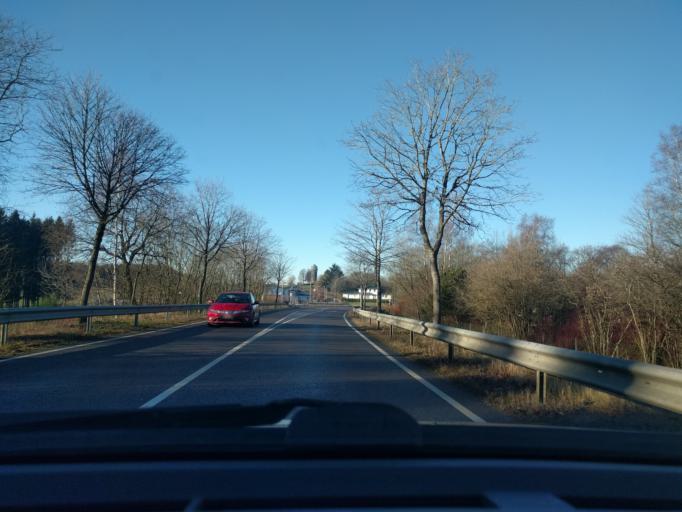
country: LU
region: Diekirch
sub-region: Canton de Clervaux
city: Weiswampach
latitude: 50.1604
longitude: 6.0310
